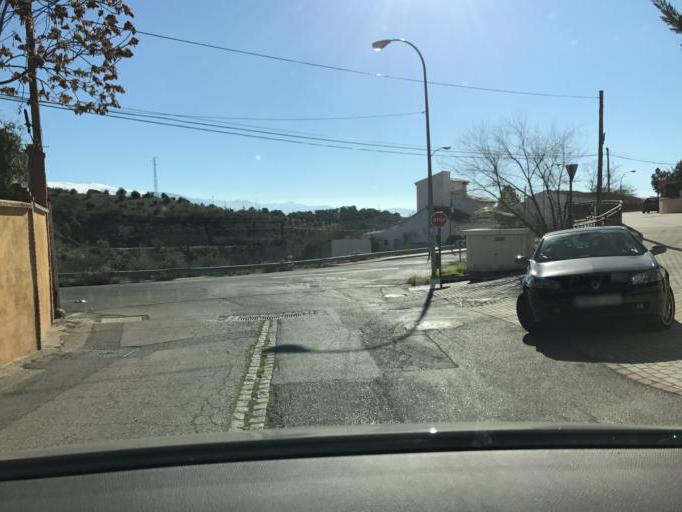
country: ES
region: Andalusia
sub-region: Provincia de Granada
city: Viznar
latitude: 37.2111
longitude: -3.5554
